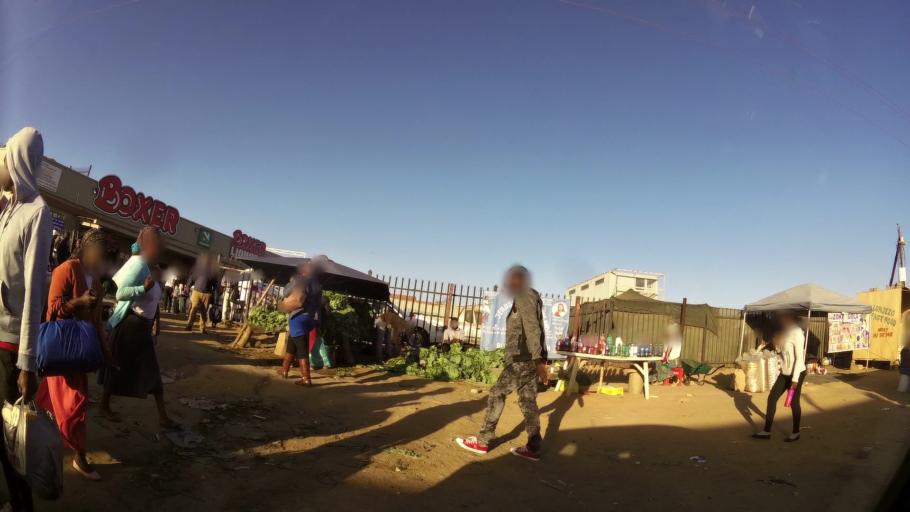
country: ZA
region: Gauteng
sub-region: City of Johannesburg Metropolitan Municipality
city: Diepsloot
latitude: -25.9355
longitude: 28.0145
